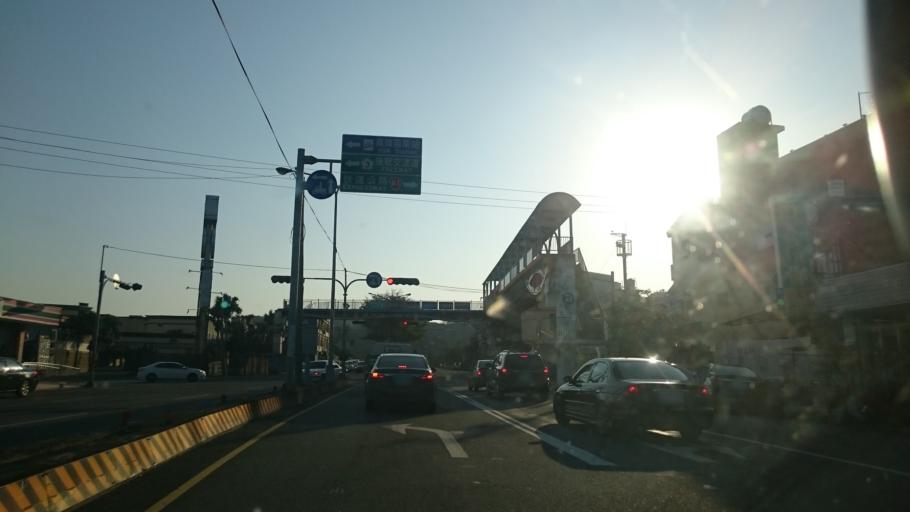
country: TW
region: Taiwan
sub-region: Miaoli
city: Miaoli
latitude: 24.6024
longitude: 120.7799
